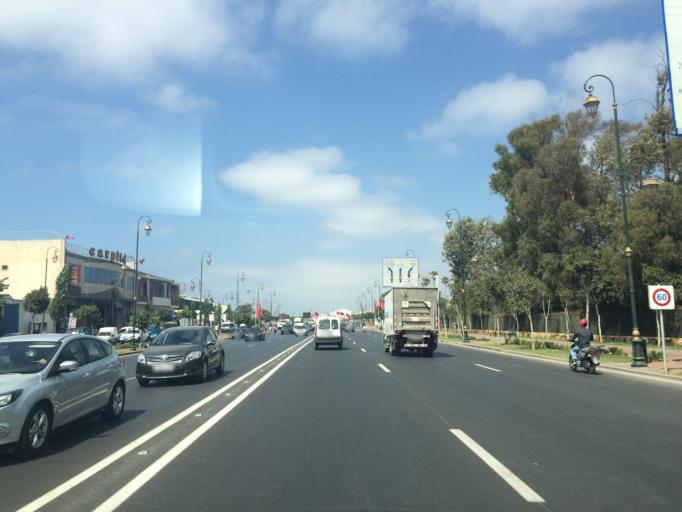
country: MA
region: Rabat-Sale-Zemmour-Zaer
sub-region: Rabat
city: Rabat
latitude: 33.9883
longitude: -6.8681
